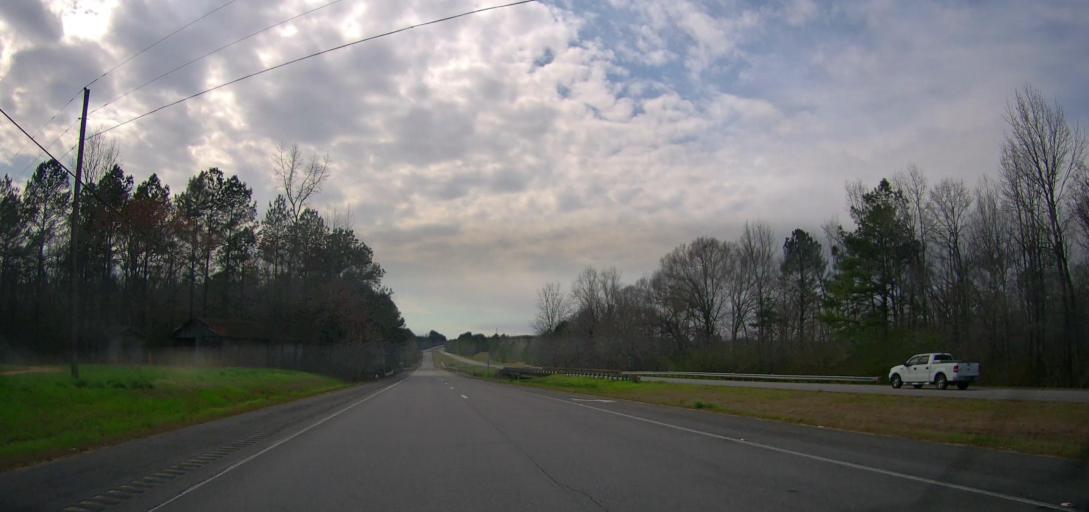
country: US
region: Alabama
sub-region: Marion County
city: Winfield
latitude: 33.9296
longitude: -87.6788
